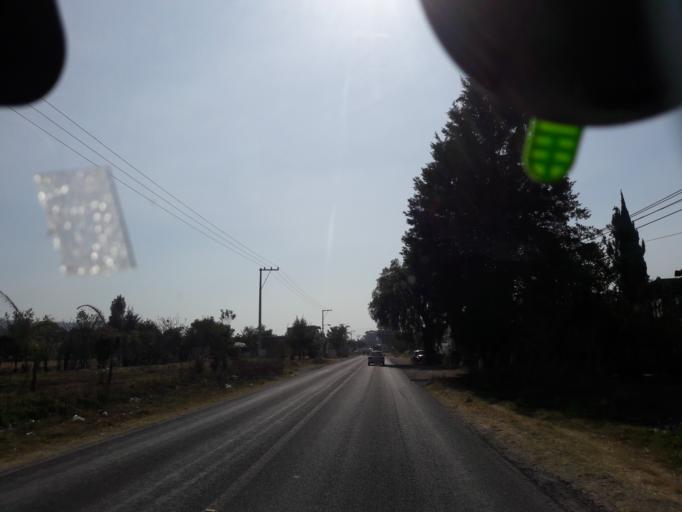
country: MX
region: Tlaxcala
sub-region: Panotla
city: Fraccionamiento la Virgen
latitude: 19.3203
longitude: -98.2851
